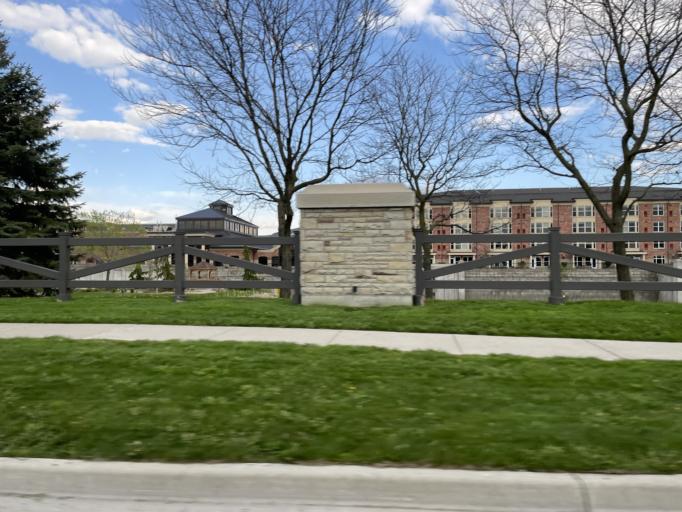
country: CA
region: Ontario
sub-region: Wellington County
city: Guelph
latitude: 43.5323
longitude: -80.2170
